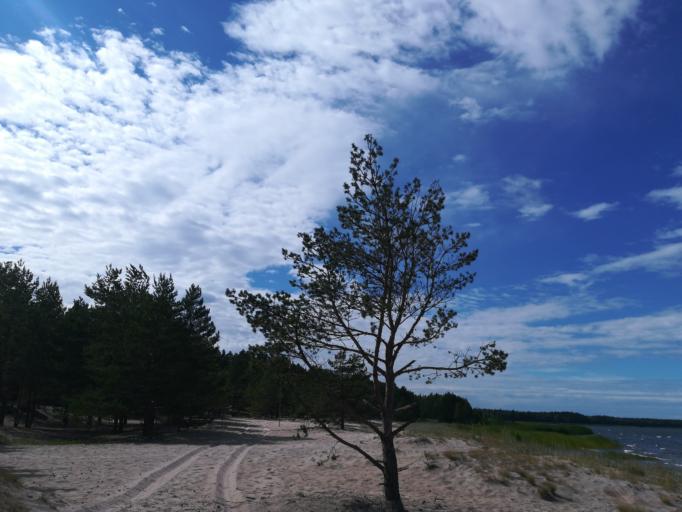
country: RU
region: Leningrad
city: Ust'-Luga
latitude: 59.6807
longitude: 28.2336
